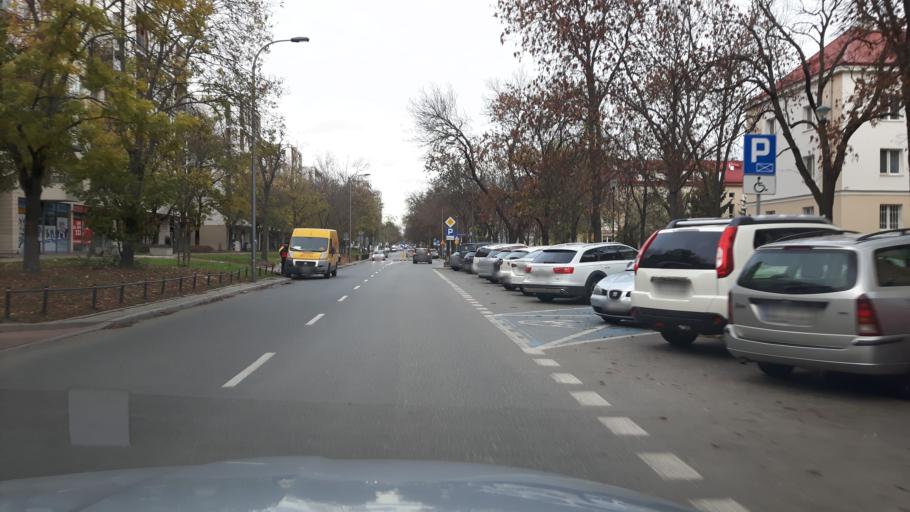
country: PL
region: Masovian Voivodeship
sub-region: Warszawa
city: Mokotow
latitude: 52.1704
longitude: 20.9980
